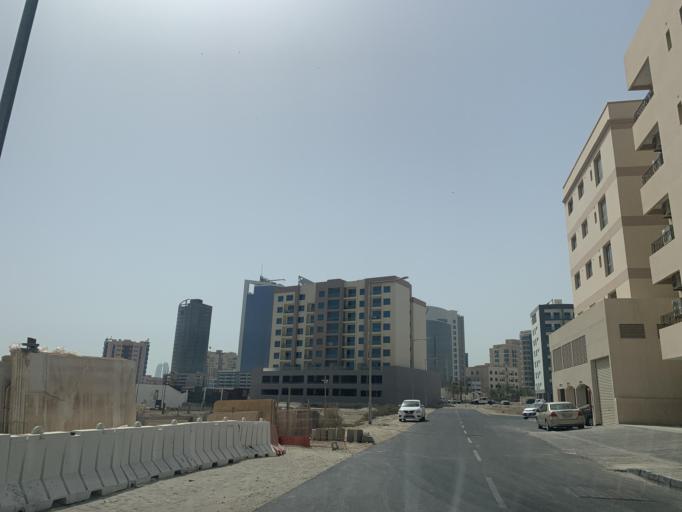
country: BH
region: Manama
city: Jidd Hafs
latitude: 26.2424
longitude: 50.5310
